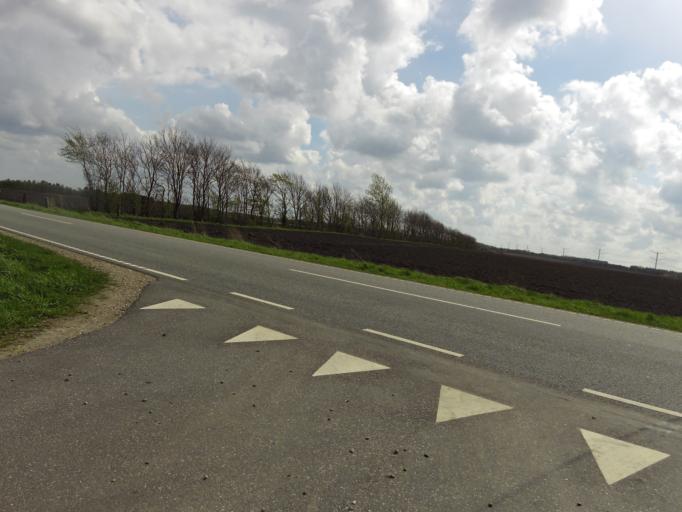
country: DK
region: South Denmark
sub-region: Tonder Kommune
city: Toftlund
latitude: 55.2039
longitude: 9.1573
